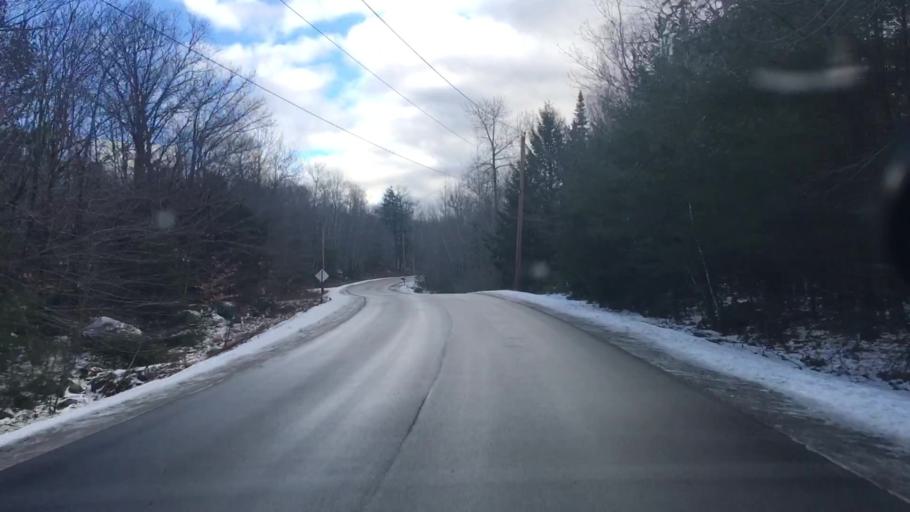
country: US
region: Maine
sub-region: Hancock County
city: Dedham
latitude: 44.6863
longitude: -68.7120
